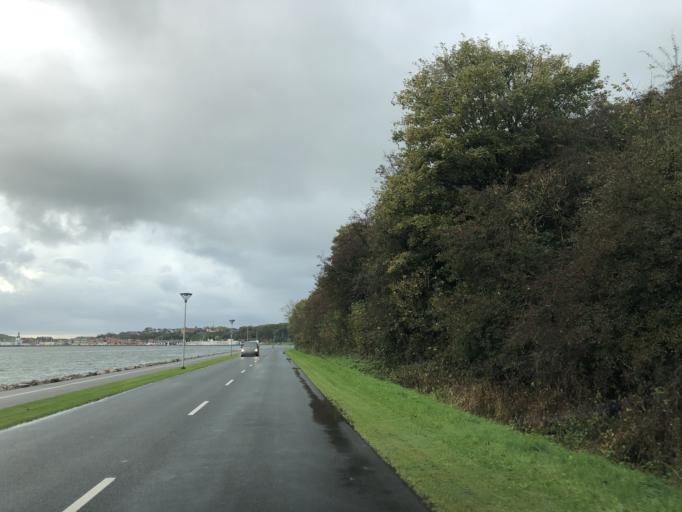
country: DK
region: Central Jutland
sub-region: Lemvig Kommune
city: Lemvig
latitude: 56.5603
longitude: 8.2947
